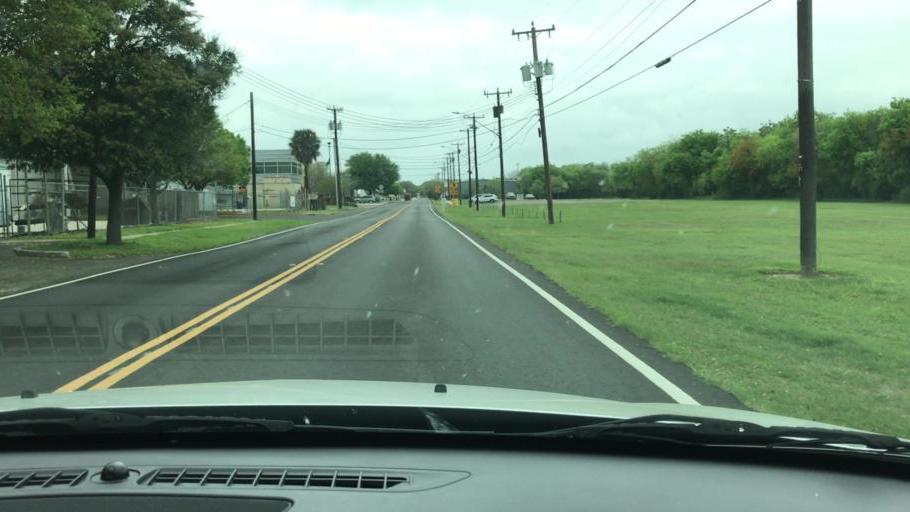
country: US
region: Texas
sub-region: Bexar County
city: San Antonio
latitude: 29.3382
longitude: -98.4666
